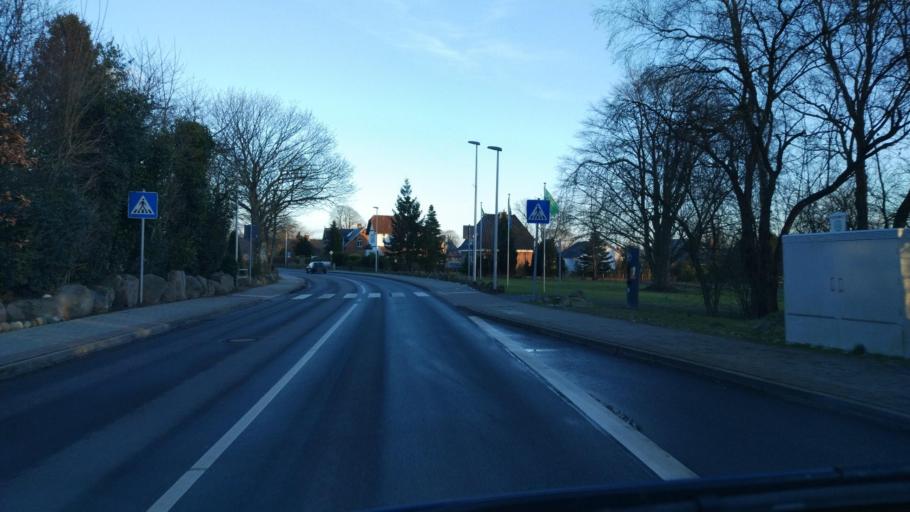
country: DE
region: Schleswig-Holstein
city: Ostenfeld
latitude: 54.4607
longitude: 9.2405
